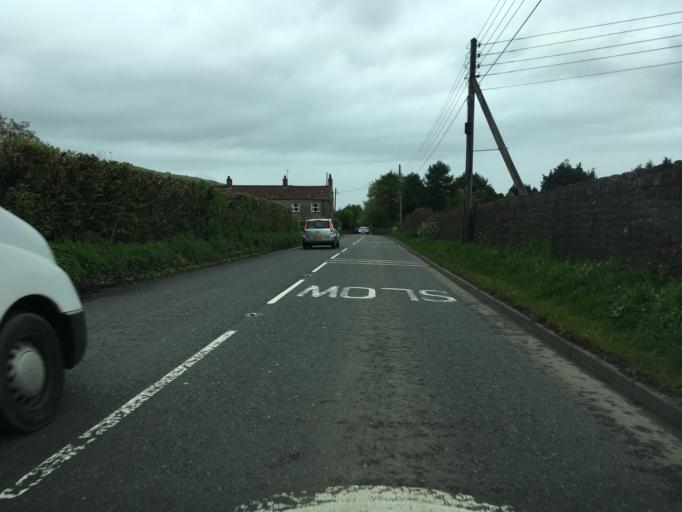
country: GB
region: England
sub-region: North Somerset
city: Churchill
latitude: 51.3333
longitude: -2.8045
